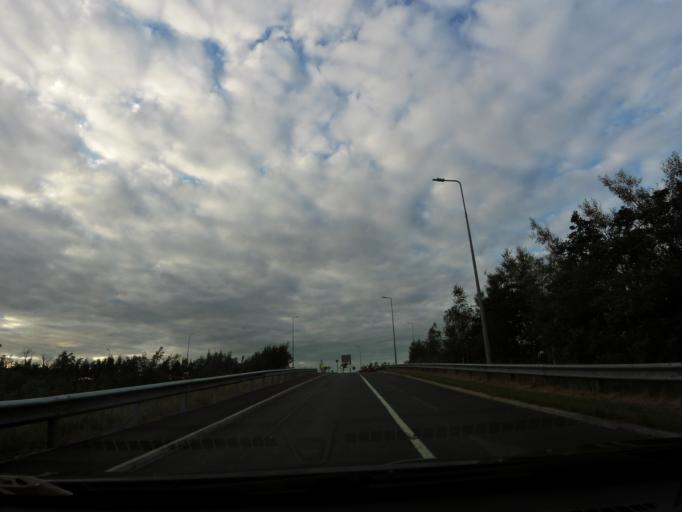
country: IE
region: Connaught
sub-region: County Galway
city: Athenry
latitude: 53.2891
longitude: -8.7555
